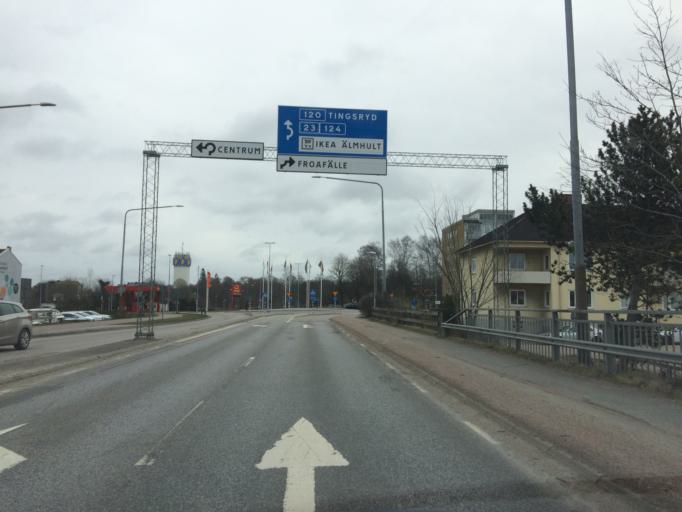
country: SE
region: Kronoberg
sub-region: Almhults Kommun
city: AElmhult
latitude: 56.5498
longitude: 14.1379
